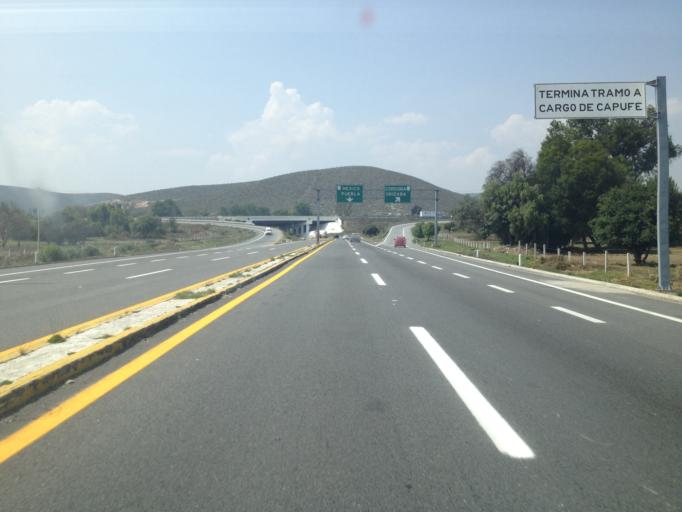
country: MX
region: Puebla
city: Cuacnopalan
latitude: 18.8239
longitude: -97.4910
